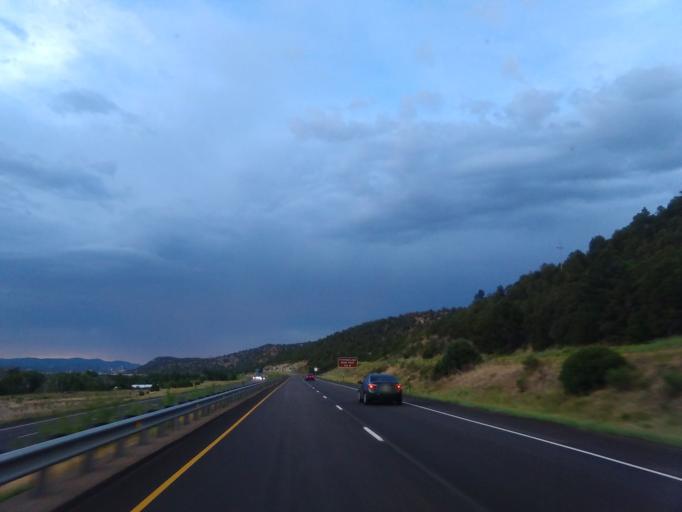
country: US
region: Colorado
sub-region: Las Animas County
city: Trinidad
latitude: 37.1078
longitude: -104.5235
